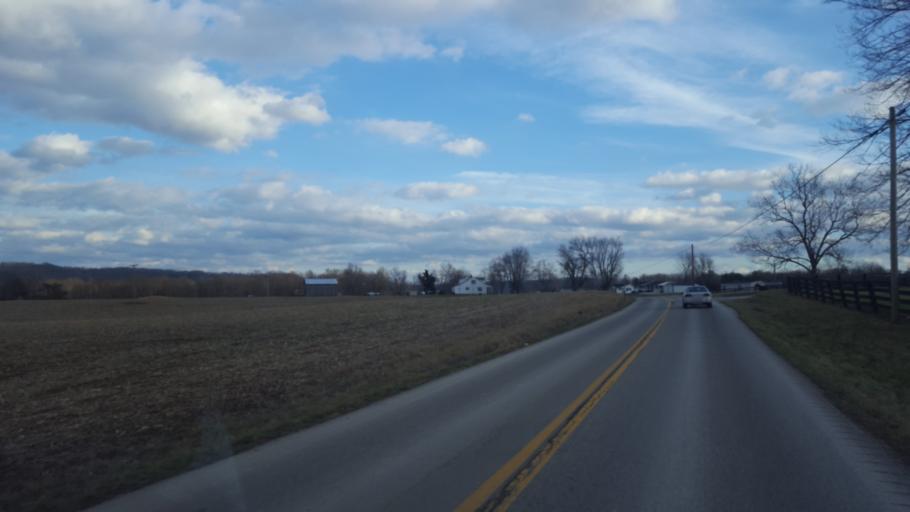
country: US
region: Kentucky
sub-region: Fleming County
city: Flemingsburg
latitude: 38.4799
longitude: -83.6069
